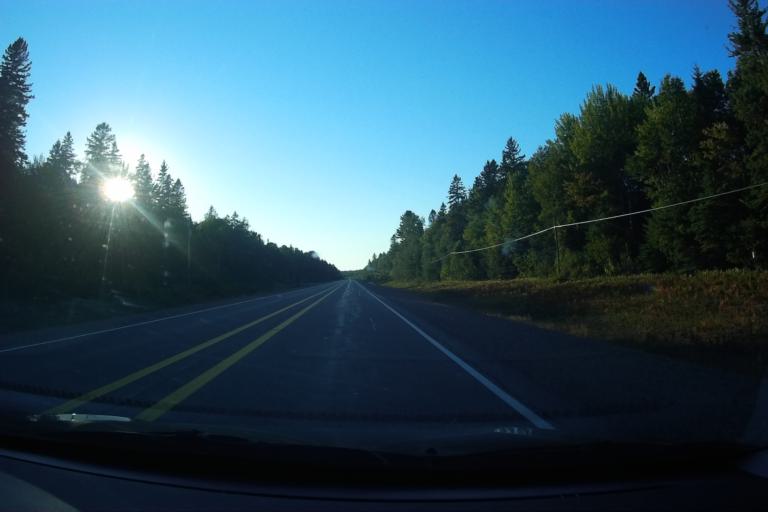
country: CA
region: Ontario
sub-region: Algoma
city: Sault Ste. Marie
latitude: 46.9655
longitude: -84.6706
